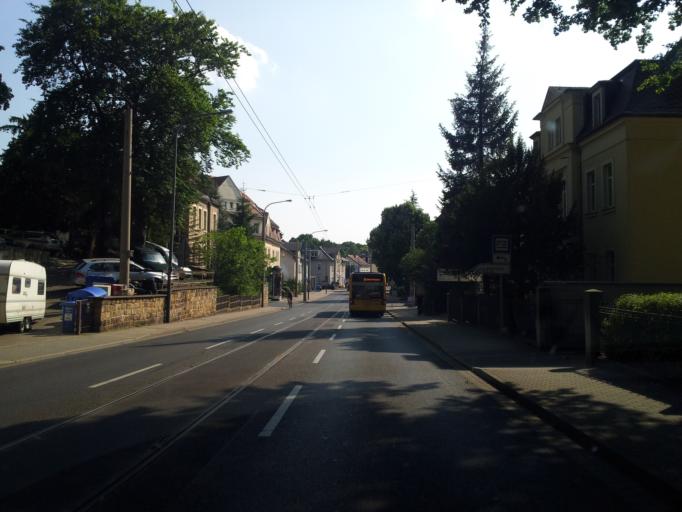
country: DE
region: Saxony
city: Albertstadt
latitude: 51.1165
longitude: 13.7874
